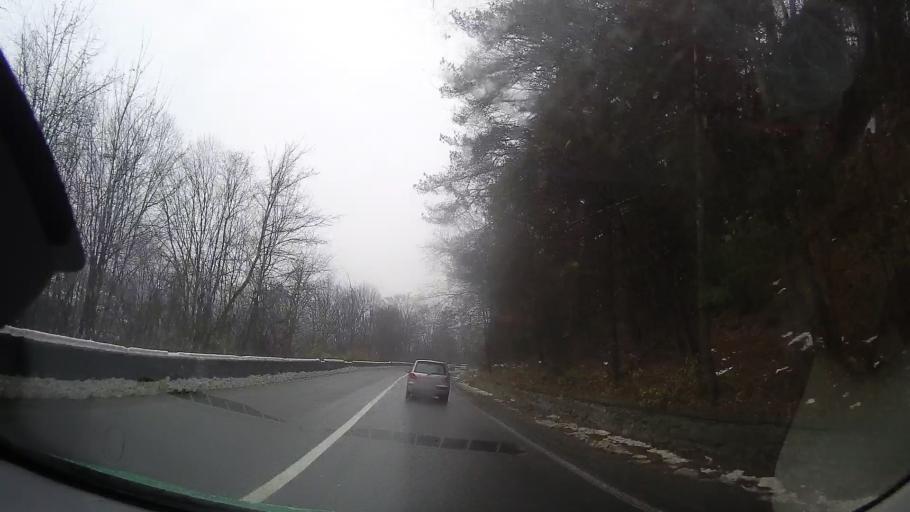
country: RO
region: Neamt
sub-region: Comuna Tarcau
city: Tarcau
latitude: 46.8981
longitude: 26.1208
